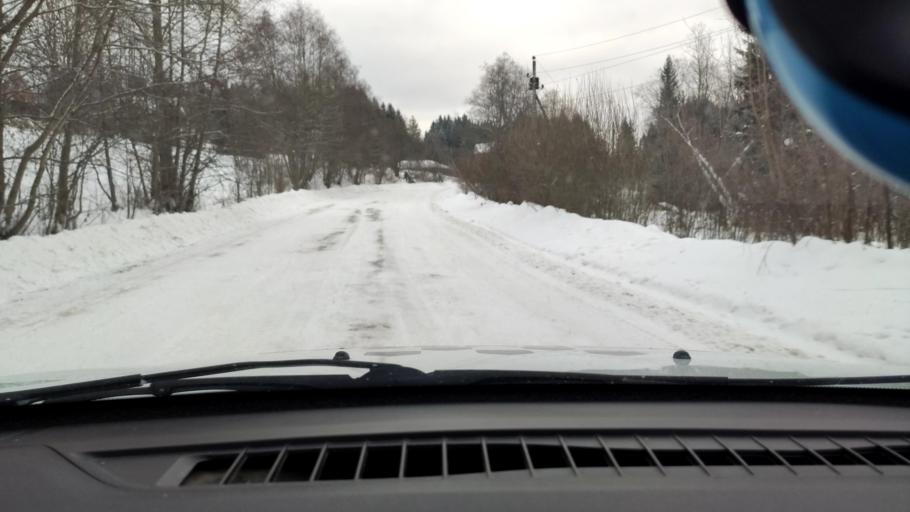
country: RU
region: Perm
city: Overyata
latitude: 58.0886
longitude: 55.9585
